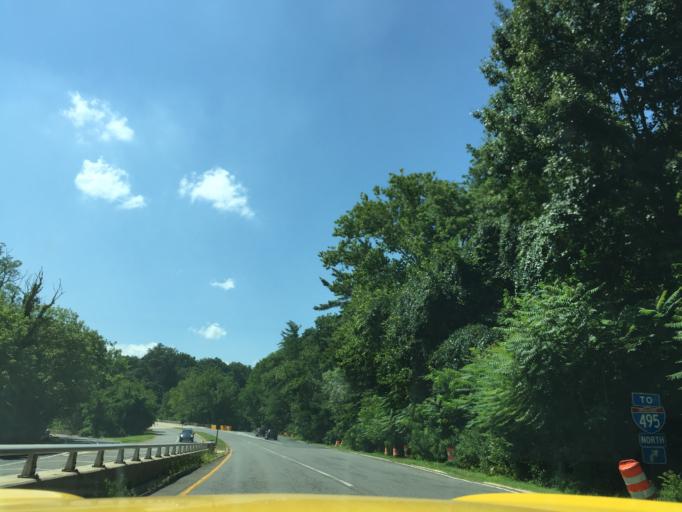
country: US
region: Maryland
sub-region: Montgomery County
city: Cabin John
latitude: 38.9700
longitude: -77.1449
